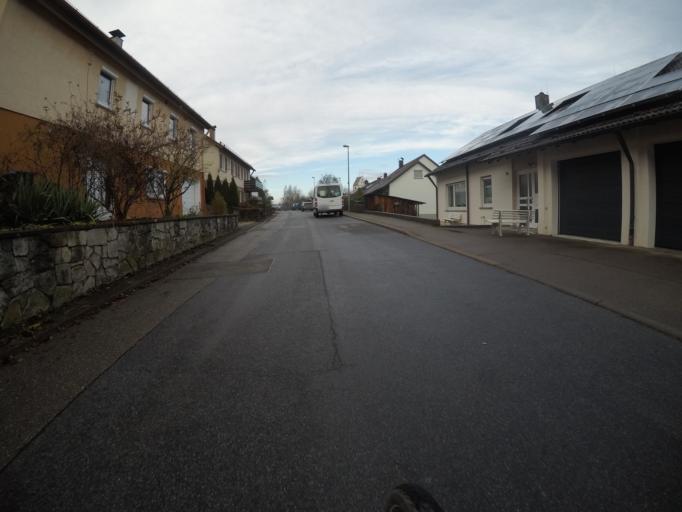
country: DE
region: Baden-Wuerttemberg
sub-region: Regierungsbezirk Stuttgart
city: Aidlingen
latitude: 48.6768
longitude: 8.9001
